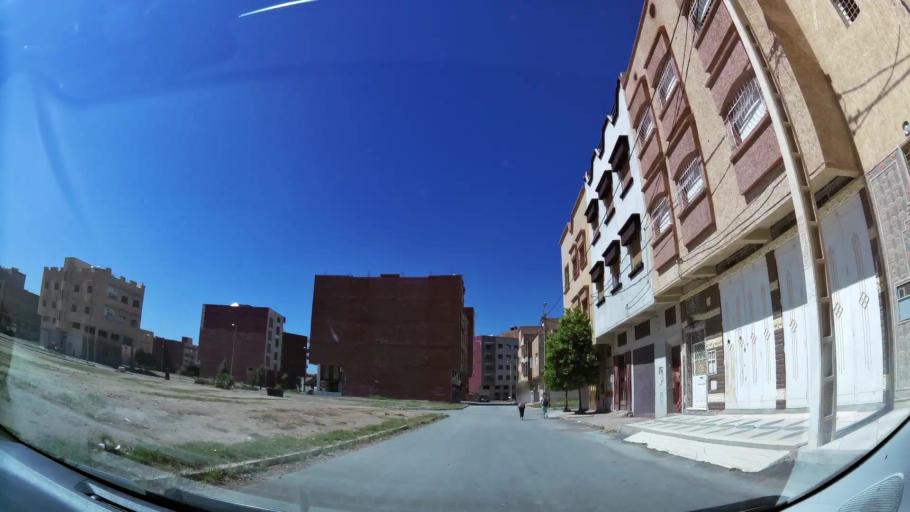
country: MA
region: Oriental
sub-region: Oujda-Angad
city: Oujda
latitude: 34.6658
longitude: -1.8745
